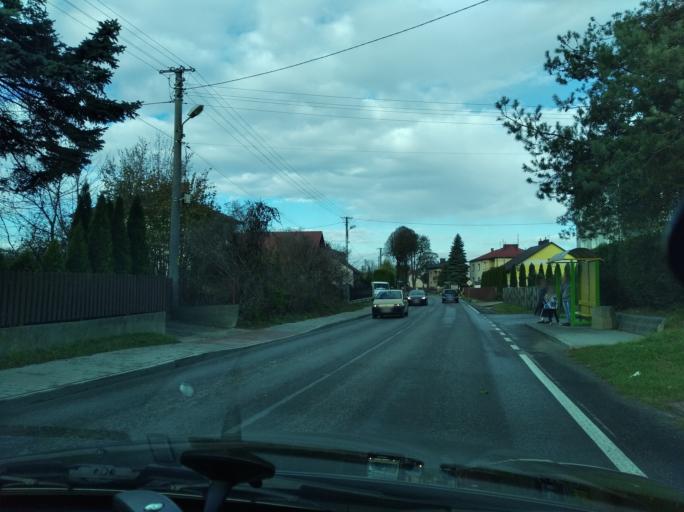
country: PL
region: Subcarpathian Voivodeship
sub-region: Powiat debicki
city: Debica
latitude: 50.0396
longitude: 21.4355
